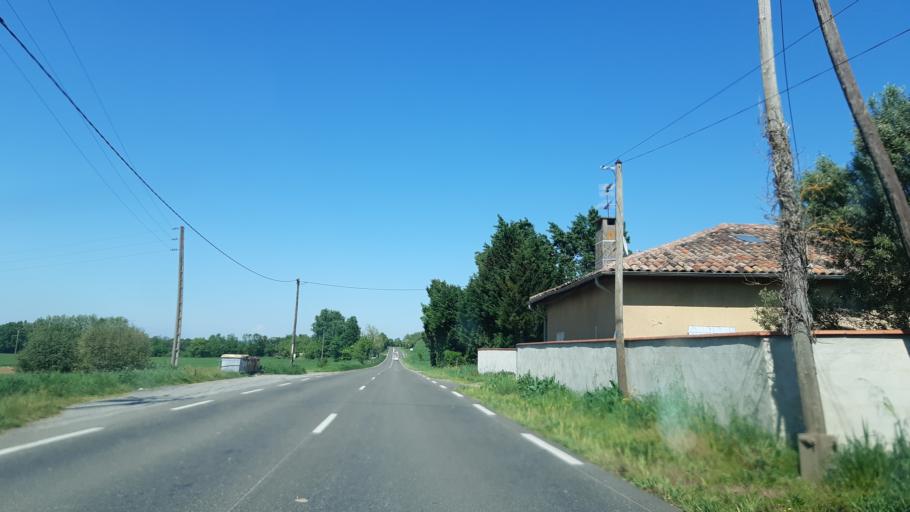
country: FR
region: Midi-Pyrenees
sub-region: Departement du Gers
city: Pujaudran
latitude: 43.5864
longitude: 1.0505
